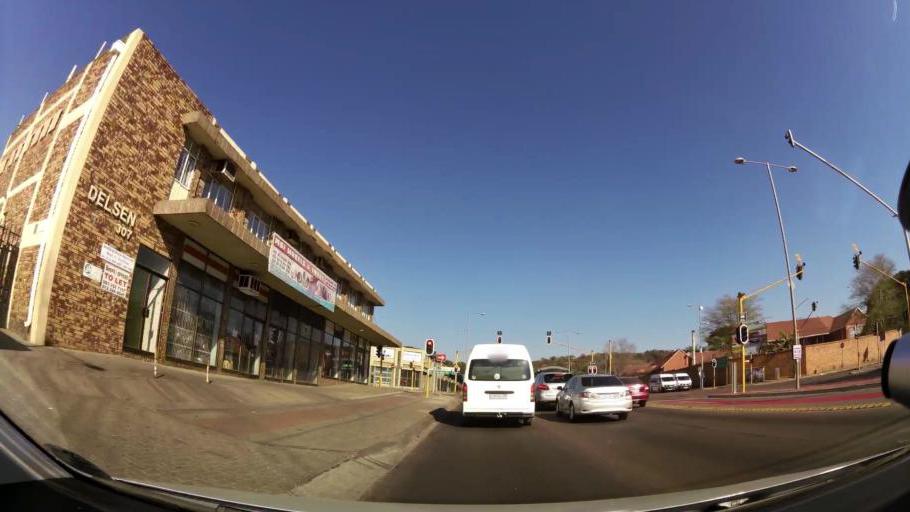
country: ZA
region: Gauteng
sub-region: City of Tshwane Metropolitan Municipality
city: Pretoria
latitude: -25.7271
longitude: 28.1887
